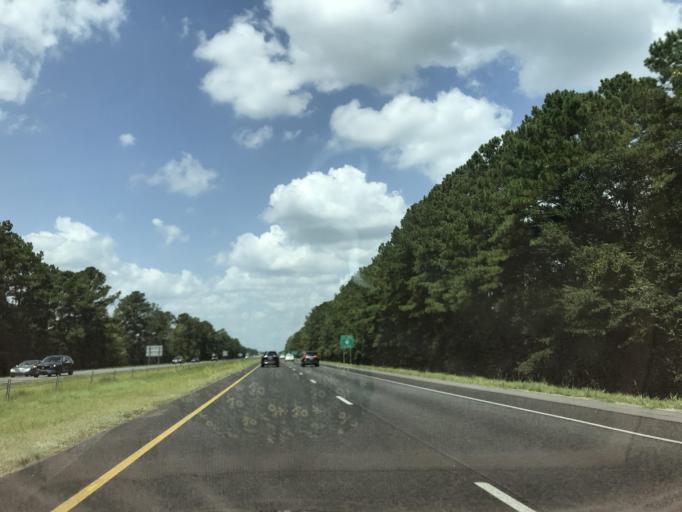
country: US
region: North Carolina
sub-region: Duplin County
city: Wallace
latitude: 34.7602
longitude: -77.9555
